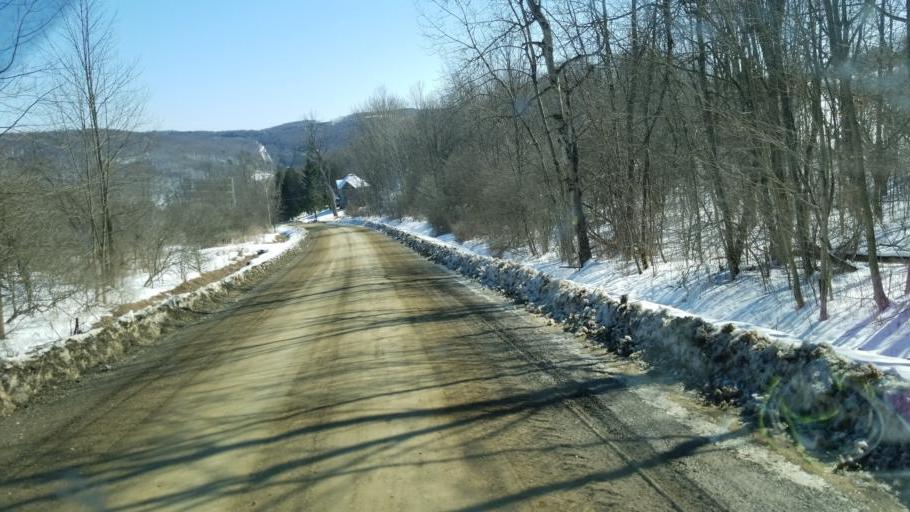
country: US
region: New York
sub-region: Allegany County
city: Andover
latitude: 42.0894
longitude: -77.6736
